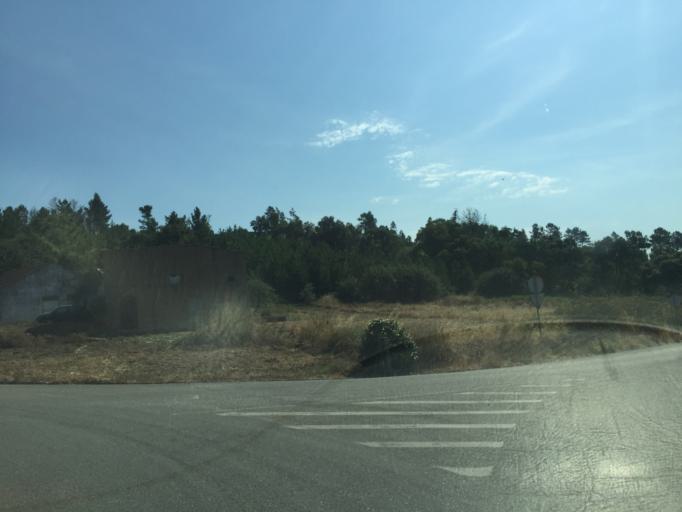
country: PT
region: Santarem
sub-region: Ferreira do Zezere
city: Ferreira do Zezere
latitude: 39.5974
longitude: -8.2931
